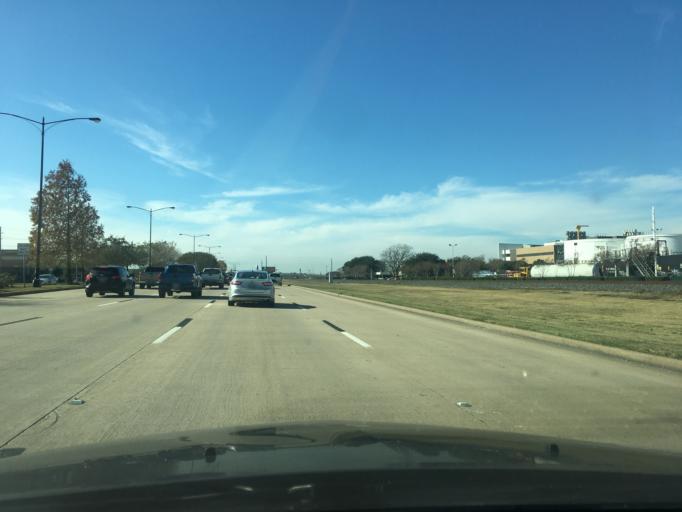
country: US
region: Texas
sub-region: Fort Bend County
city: Sugar Land
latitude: 29.6182
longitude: -95.6402
